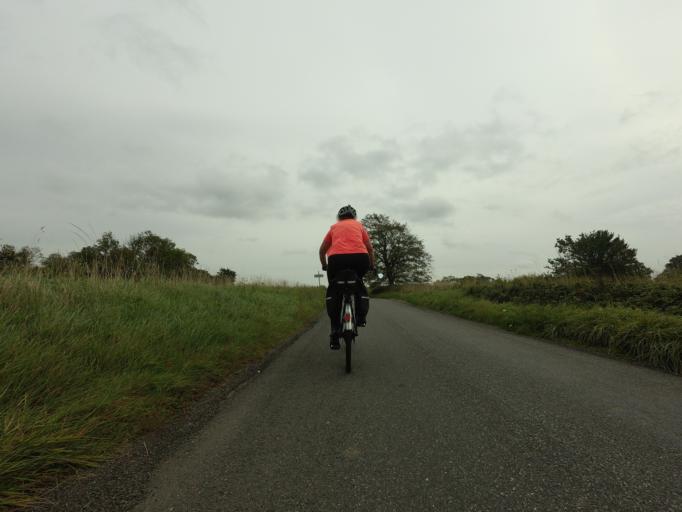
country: GB
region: England
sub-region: Hertfordshire
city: Buntingford
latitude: 51.9767
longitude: 0.0678
